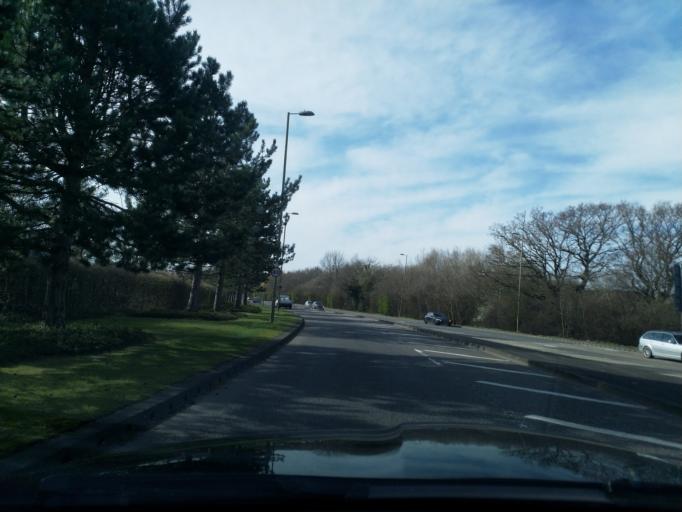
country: GB
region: England
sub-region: Hampshire
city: Farnborough
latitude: 51.2838
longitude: -0.7719
